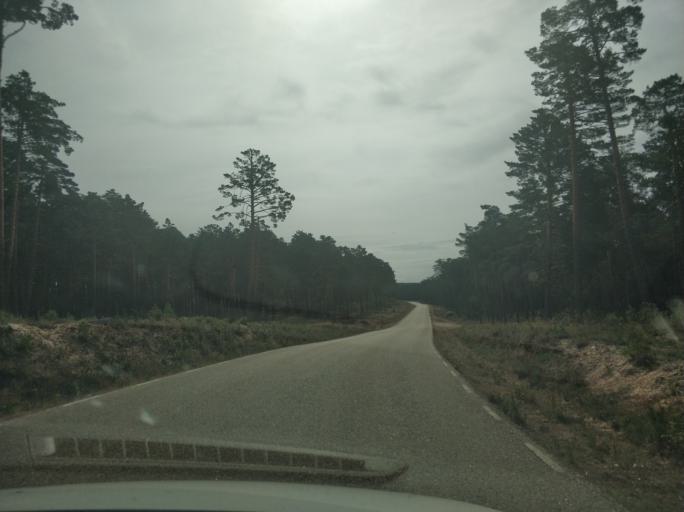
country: ES
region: Castille and Leon
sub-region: Provincia de Soria
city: Navaleno
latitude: 41.8572
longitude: -2.9687
